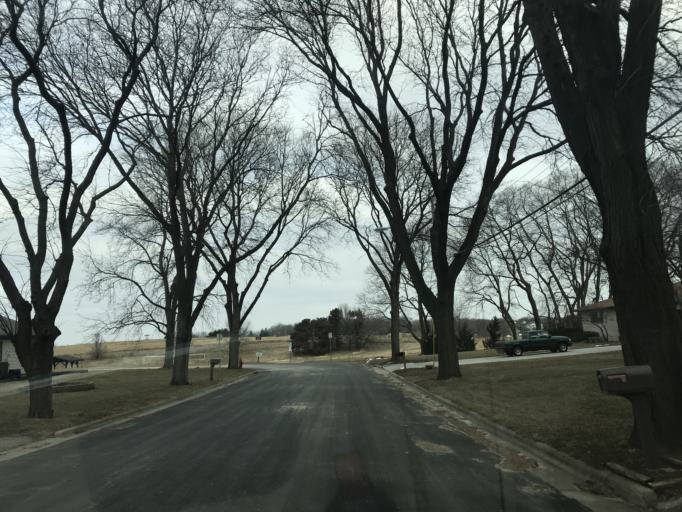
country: US
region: Wisconsin
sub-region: Dane County
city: Monona
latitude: 43.1096
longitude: -89.3022
